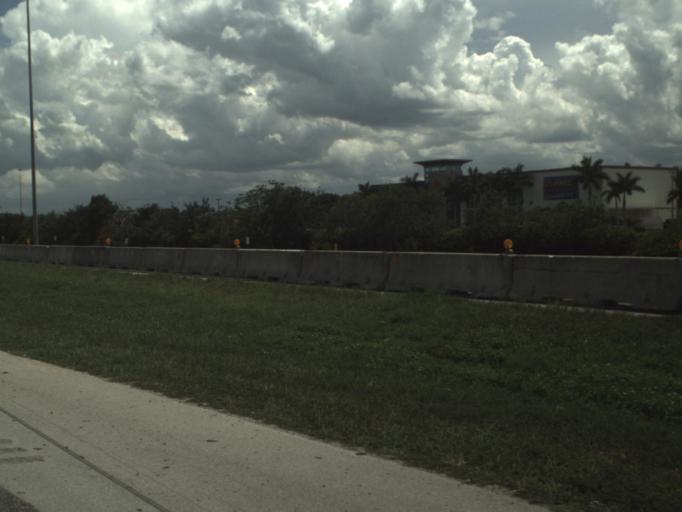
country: US
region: Florida
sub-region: Broward County
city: Sunshine Ranches
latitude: 26.0352
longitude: -80.3529
